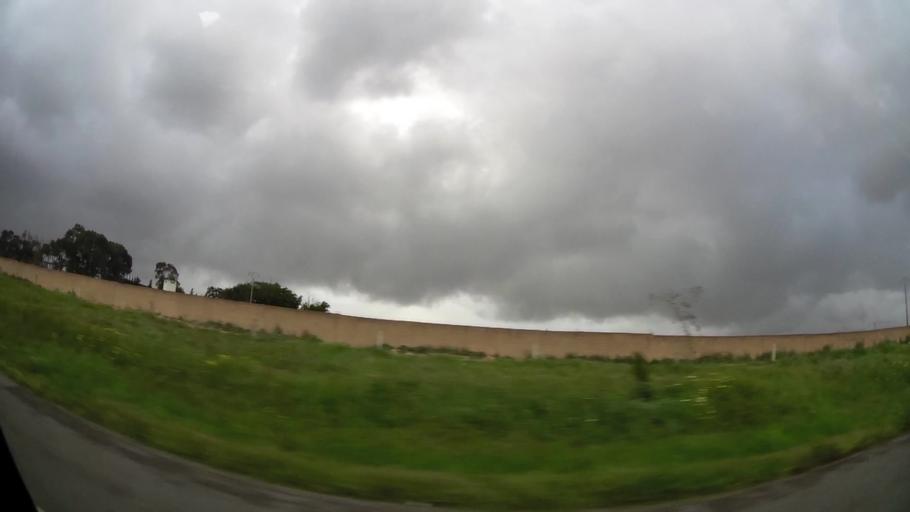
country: MA
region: Grand Casablanca
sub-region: Mediouna
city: Tit Mellil
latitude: 33.5654
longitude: -7.4865
